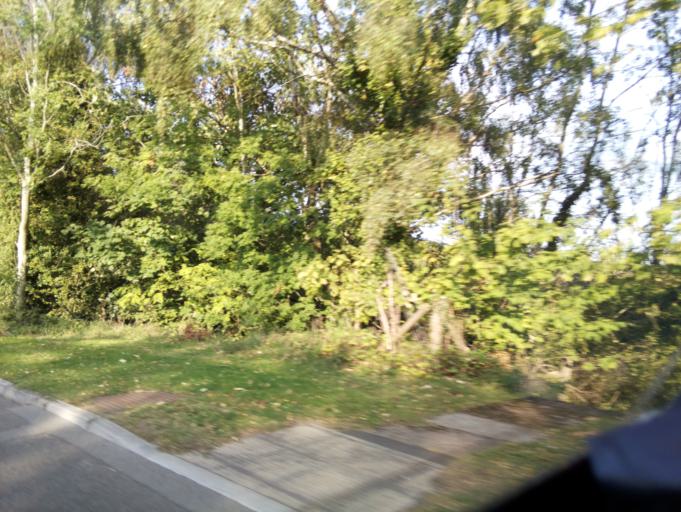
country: GB
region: Wales
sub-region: Torfaen County Borough
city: Cwmbran
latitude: 51.6562
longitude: -3.0451
